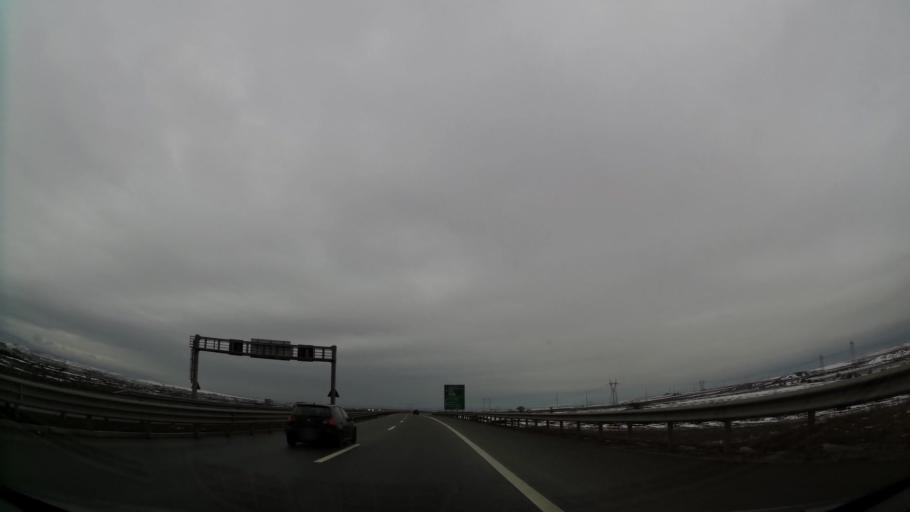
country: XK
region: Pristina
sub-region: Kosovo Polje
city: Kosovo Polje
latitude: 42.6224
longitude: 21.1274
